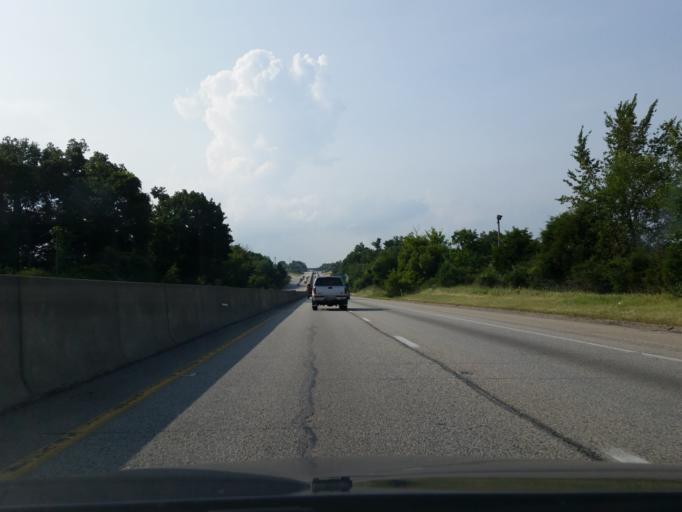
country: US
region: Pennsylvania
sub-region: York County
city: Manchester
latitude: 40.0741
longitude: -76.7601
